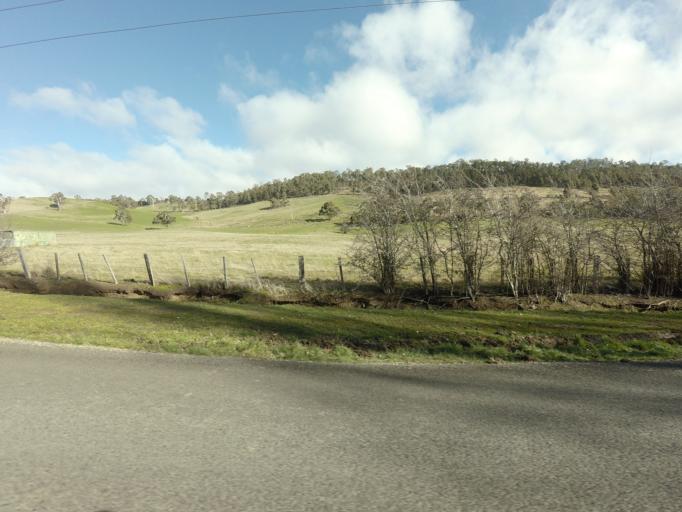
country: AU
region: Tasmania
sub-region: Derwent Valley
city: New Norfolk
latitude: -42.6117
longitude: 146.7117
